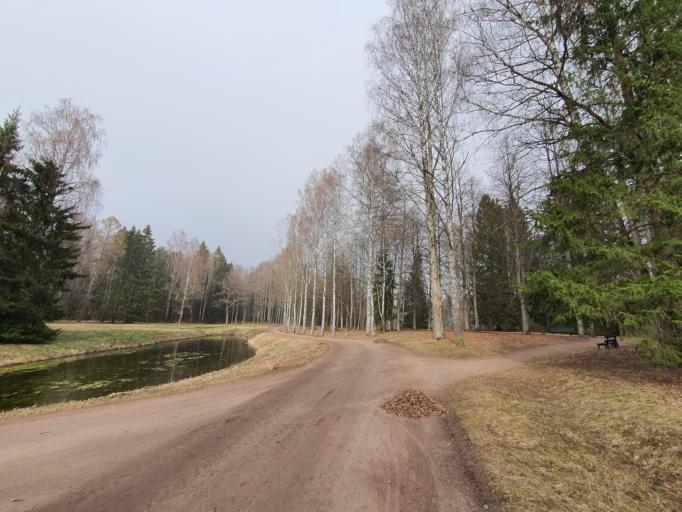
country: RU
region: St.-Petersburg
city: Tyarlevo
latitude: 59.6912
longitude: 30.4548
